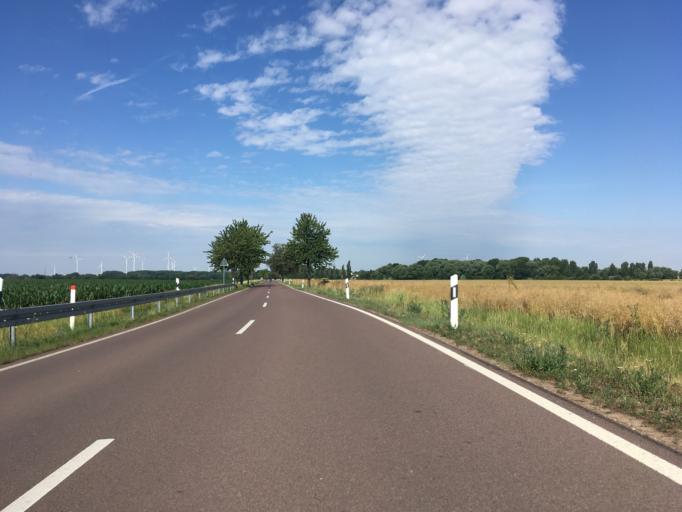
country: DE
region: Saxony-Anhalt
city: Wulfen
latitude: 51.7715
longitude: 11.8940
